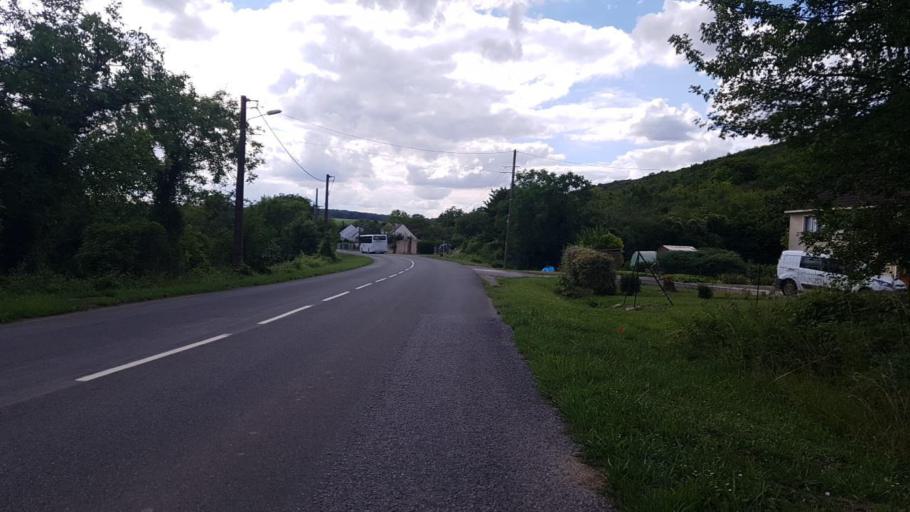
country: FR
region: Picardie
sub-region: Departement de l'Aisne
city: Crezancy
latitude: 49.0742
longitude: 3.5144
